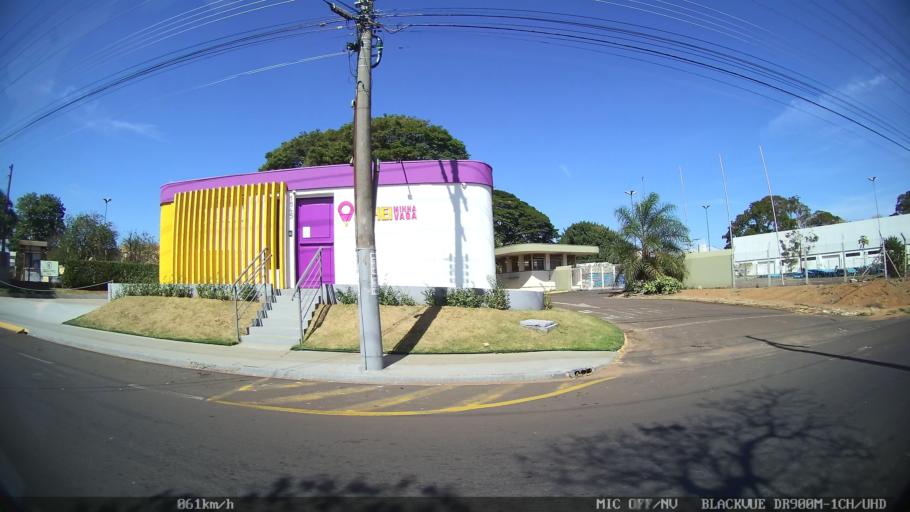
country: BR
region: Sao Paulo
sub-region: Franca
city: Franca
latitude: -20.5452
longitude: -47.4275
